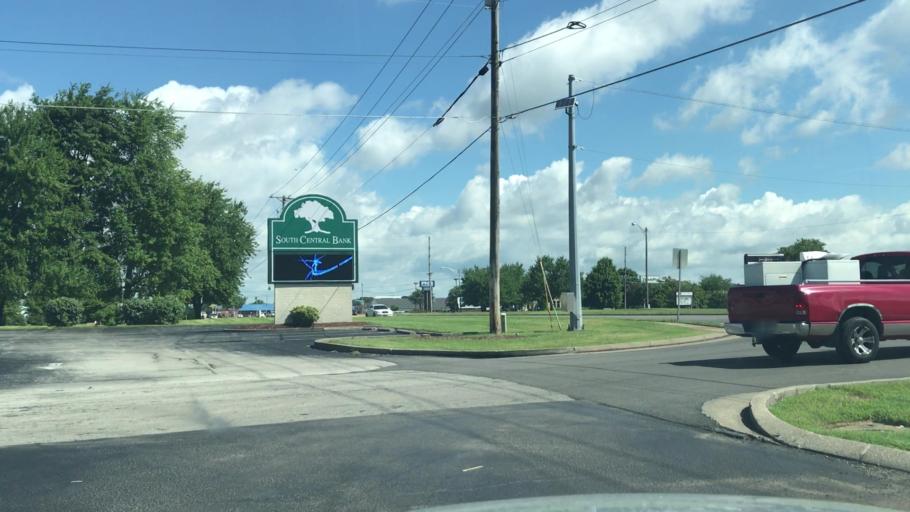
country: US
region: Kentucky
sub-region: Warren County
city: Plano
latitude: 36.9242
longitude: -86.4109
